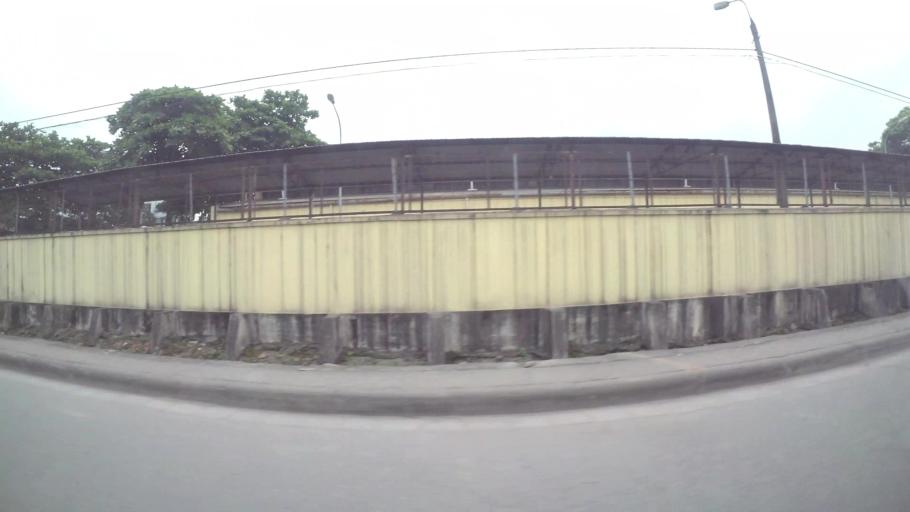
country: VN
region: Ha Noi
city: Hoan Kiem
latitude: 21.0666
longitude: 105.8848
